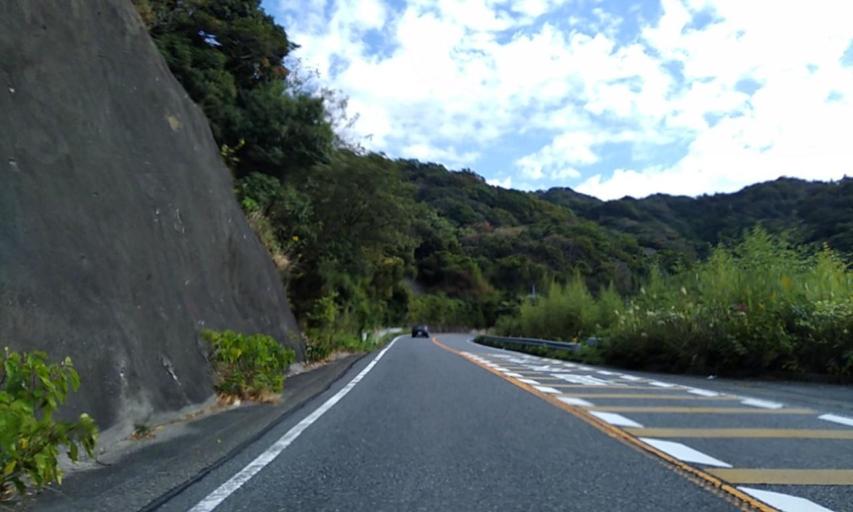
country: JP
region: Wakayama
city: Gobo
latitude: 33.9541
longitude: 135.1239
